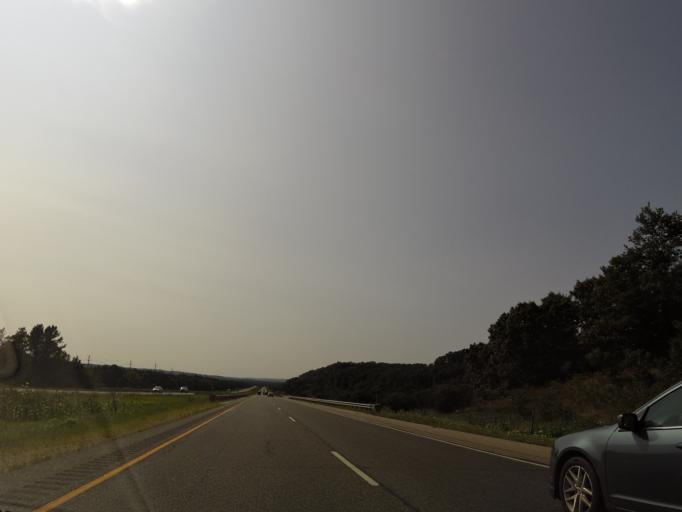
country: US
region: Wisconsin
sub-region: Monroe County
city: Tomah
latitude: 43.9395
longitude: -90.6217
